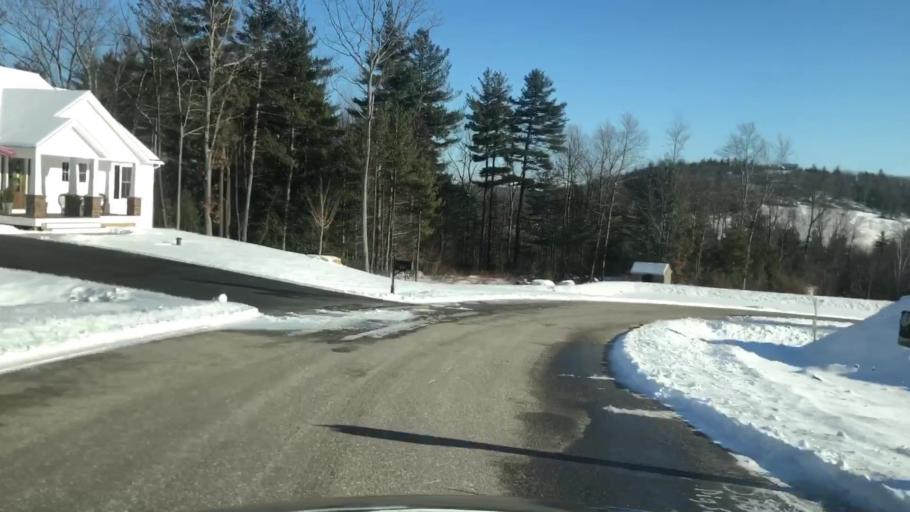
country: US
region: New Hampshire
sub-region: Hillsborough County
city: Wilton
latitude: 42.8025
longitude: -71.7091
